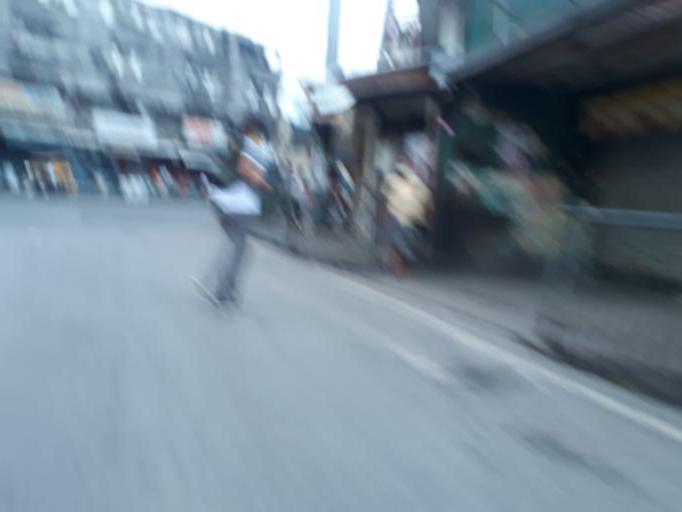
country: PH
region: Calabarzon
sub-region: Province of Rizal
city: Valenzuela
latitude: 14.6923
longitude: 120.9638
